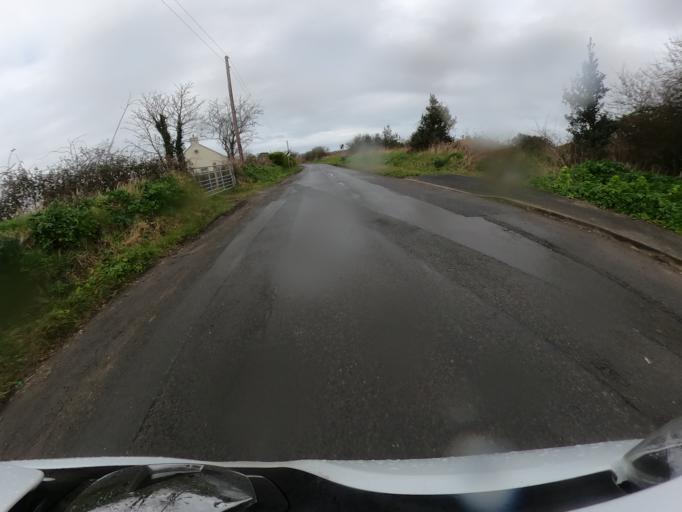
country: IM
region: Ramsey
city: Ramsey
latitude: 54.3695
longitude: -4.4465
